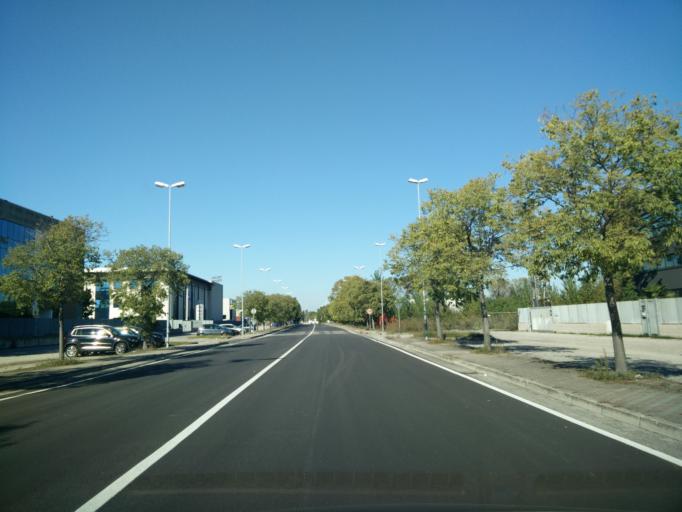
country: IT
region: Veneto
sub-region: Provincia di Venezia
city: Mestre
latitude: 45.4587
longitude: 12.2173
